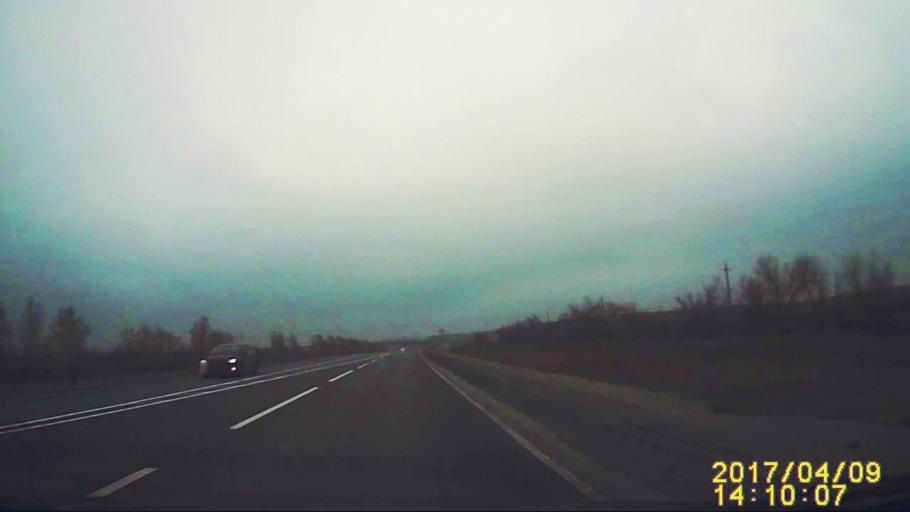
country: RU
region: Ulyanovsk
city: Krasnyy Gulyay
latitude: 54.0352
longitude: 48.2129
